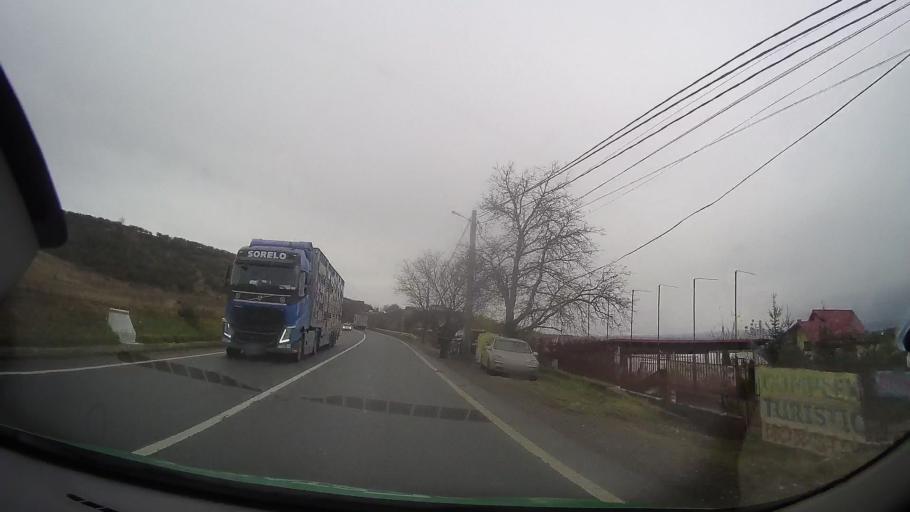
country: RO
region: Mures
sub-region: Comuna Breaza
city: Breaza
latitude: 46.7695
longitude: 24.6578
